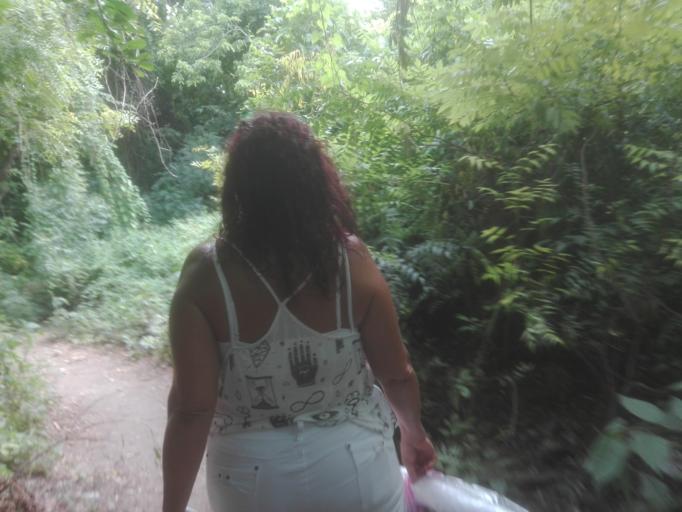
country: CO
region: Bolivar
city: Turbana
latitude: 10.1758
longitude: -75.7422
